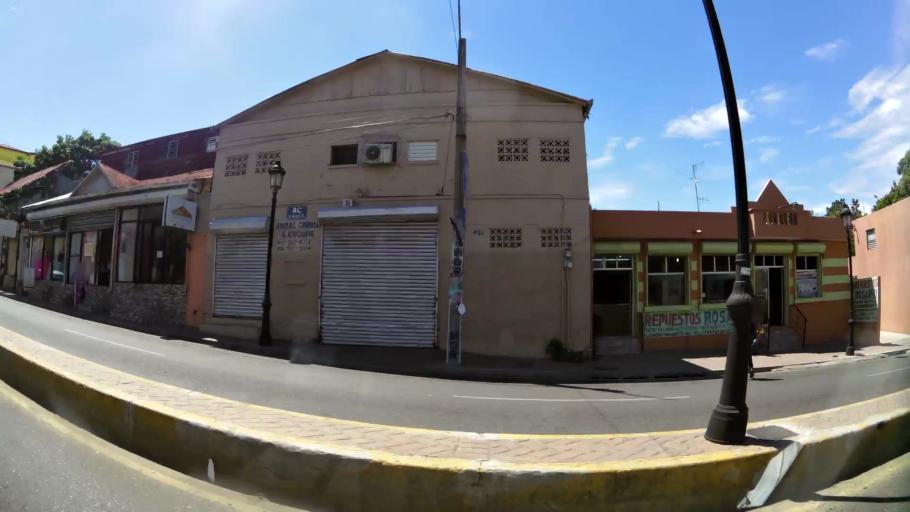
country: DO
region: Santiago
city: Santiago de los Caballeros
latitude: 19.4546
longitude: -70.7076
